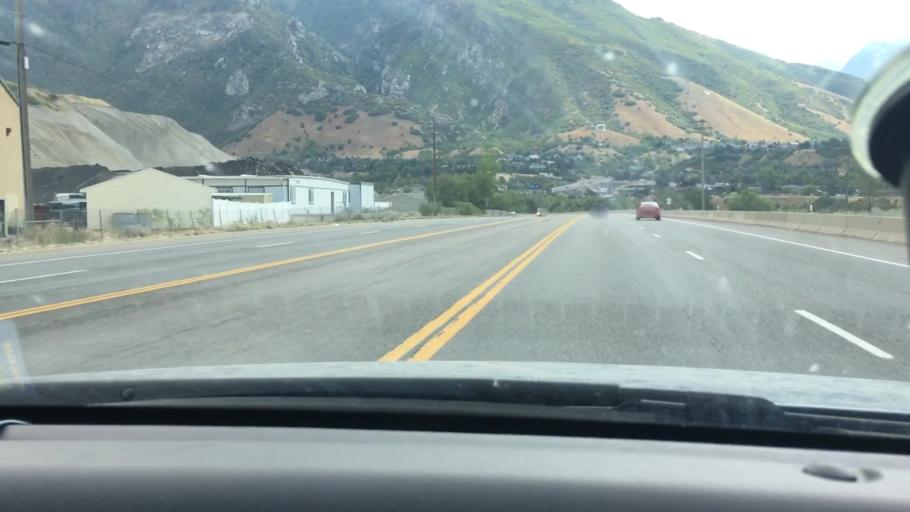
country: US
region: Utah
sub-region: Salt Lake County
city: Cottonwood Heights
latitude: 40.6260
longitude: -111.7971
